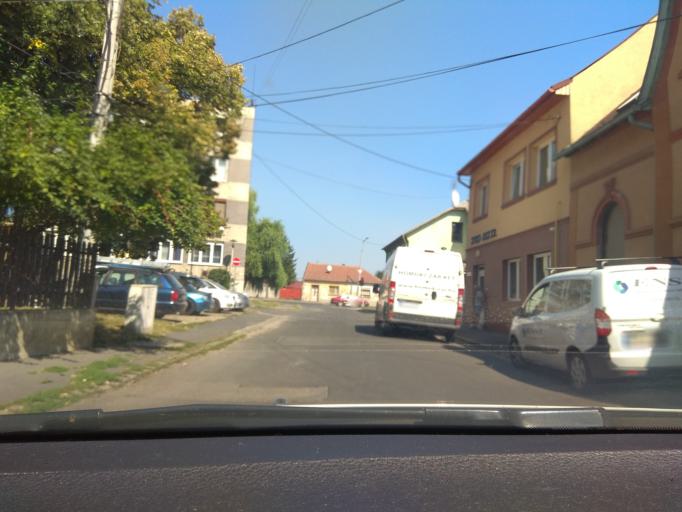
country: HU
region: Borsod-Abauj-Zemplen
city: Miskolc
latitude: 48.0733
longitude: 20.7871
